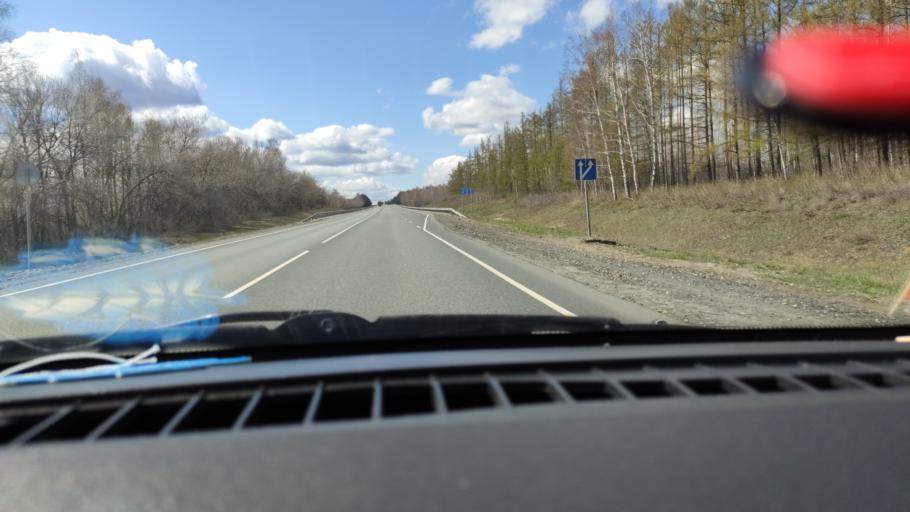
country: RU
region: Saratov
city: Khvalynsk
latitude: 52.5641
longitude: 48.0931
